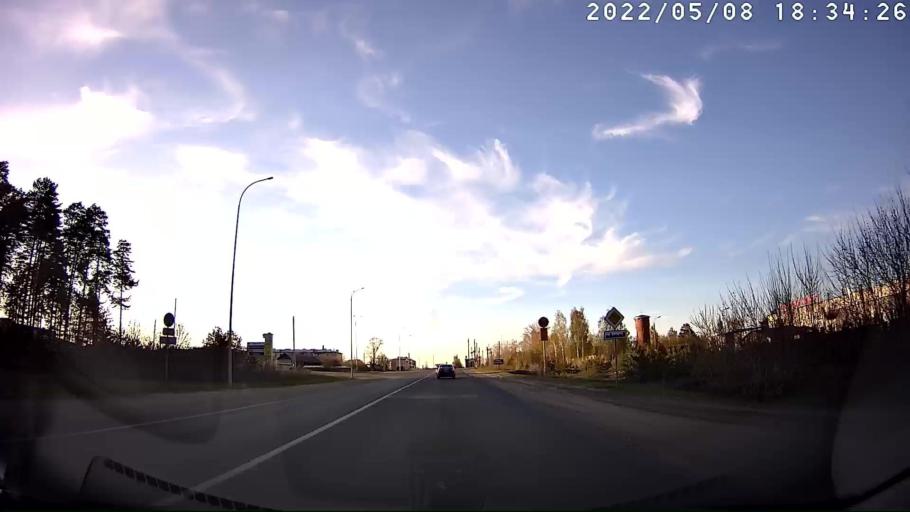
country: RU
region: Mariy-El
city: Volzhsk
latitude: 55.9001
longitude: 48.3563
